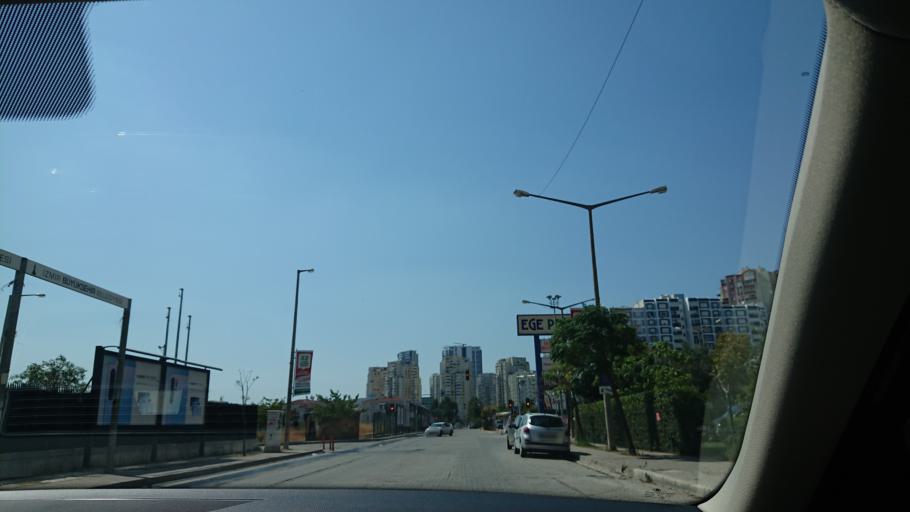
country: TR
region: Izmir
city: Karsiyaka
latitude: 38.4696
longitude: 27.0763
